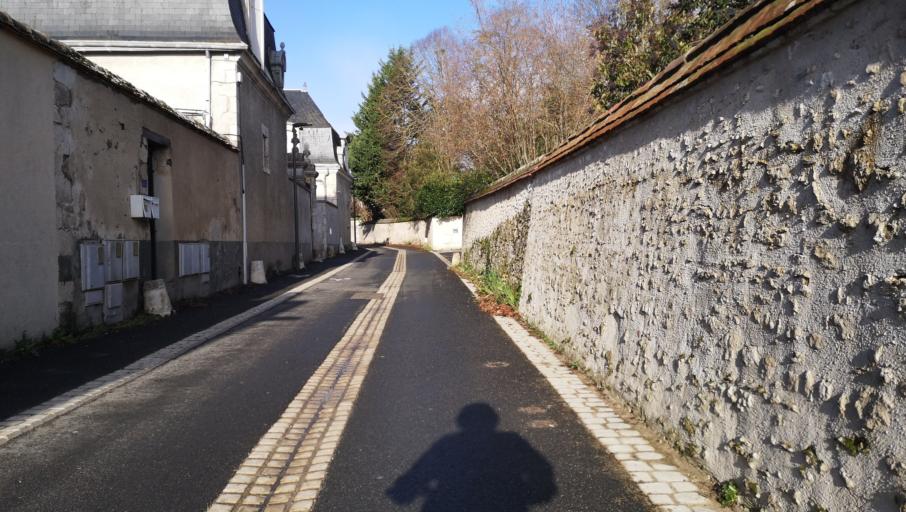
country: FR
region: Centre
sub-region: Departement du Loiret
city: Saint-Pryve-Saint-Mesmin
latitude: 47.8908
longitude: 1.8760
